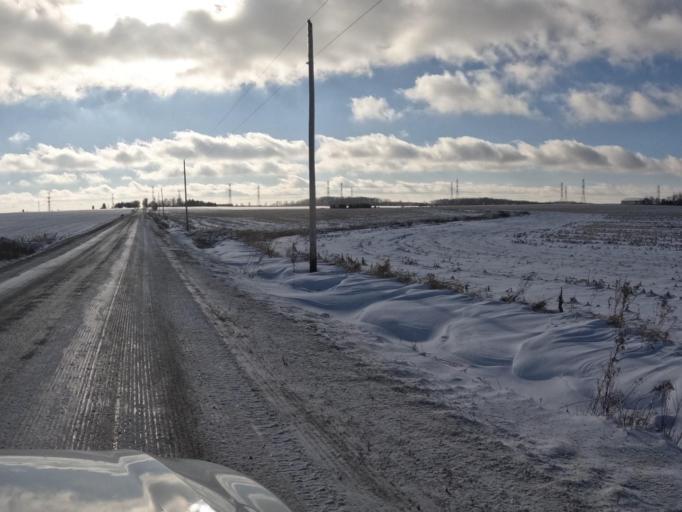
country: CA
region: Ontario
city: Shelburne
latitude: 44.0057
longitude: -80.4107
